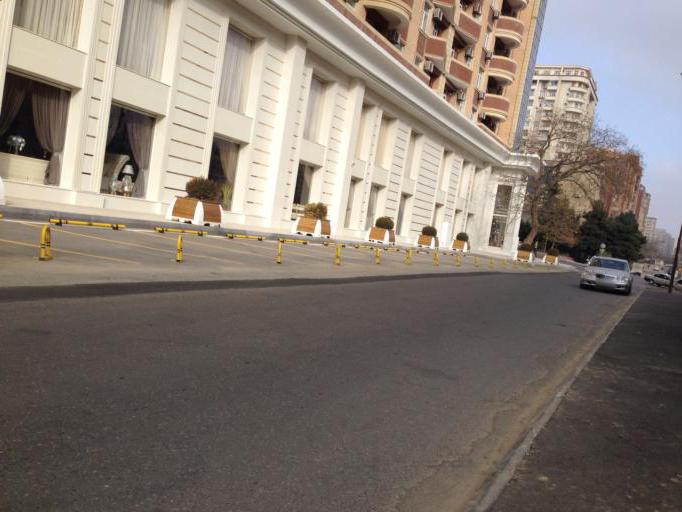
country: AZ
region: Baki
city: Baku
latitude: 40.3966
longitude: 49.8591
